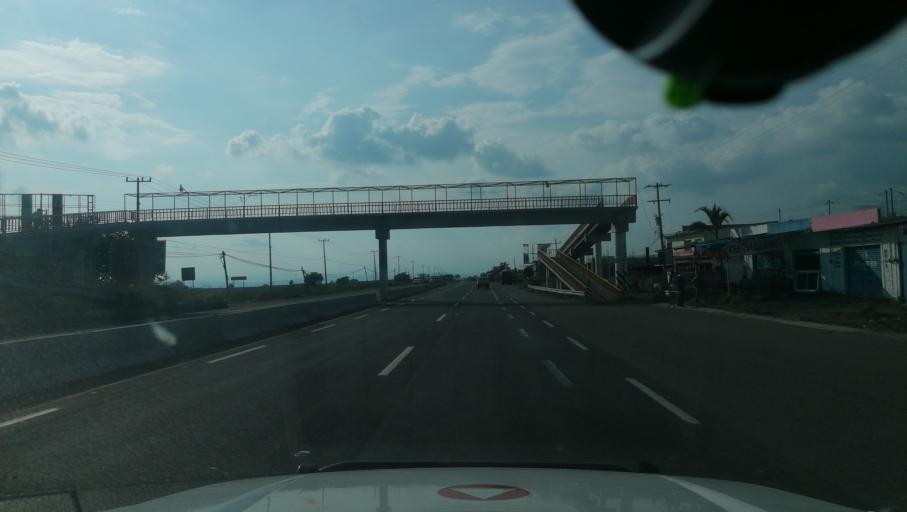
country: MX
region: Morelos
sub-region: Ayala
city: Unidad Habitacional Mariano Matamoros
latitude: 18.7515
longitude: -98.8529
